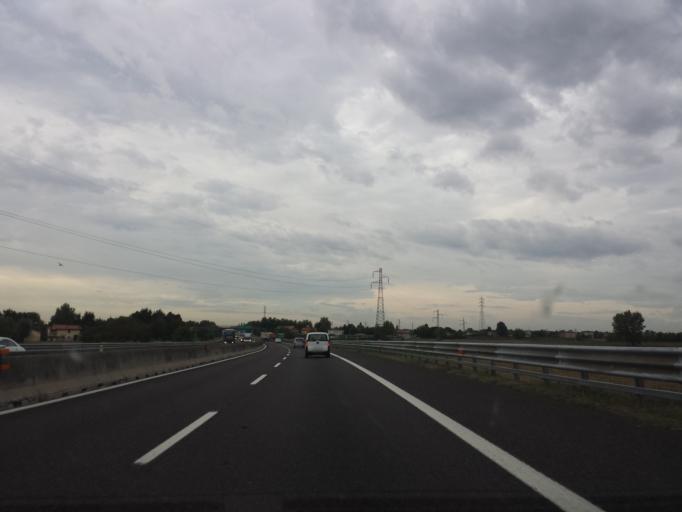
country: IT
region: Veneto
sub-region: Provincia di Padova
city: Pernumia
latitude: 45.2524
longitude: 11.7746
